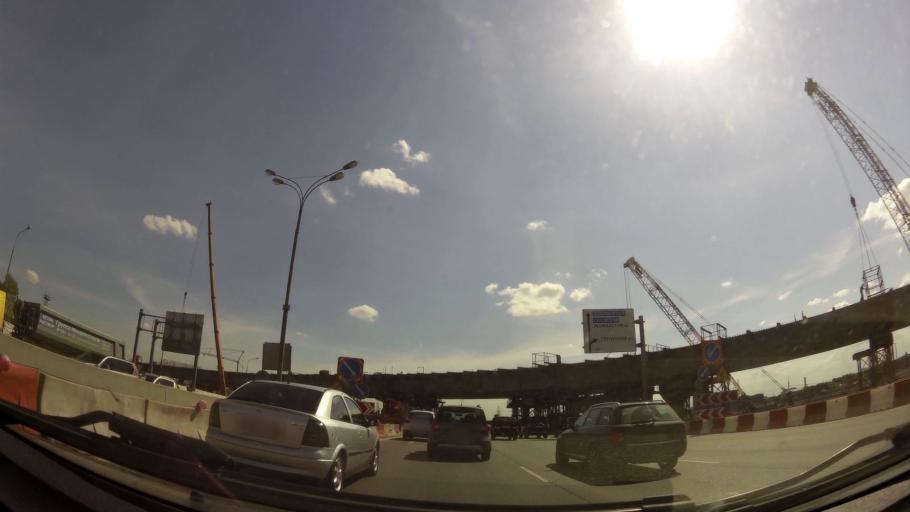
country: RU
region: Moskovskaya
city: Nemchinovka
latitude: 55.7303
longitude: 37.3772
